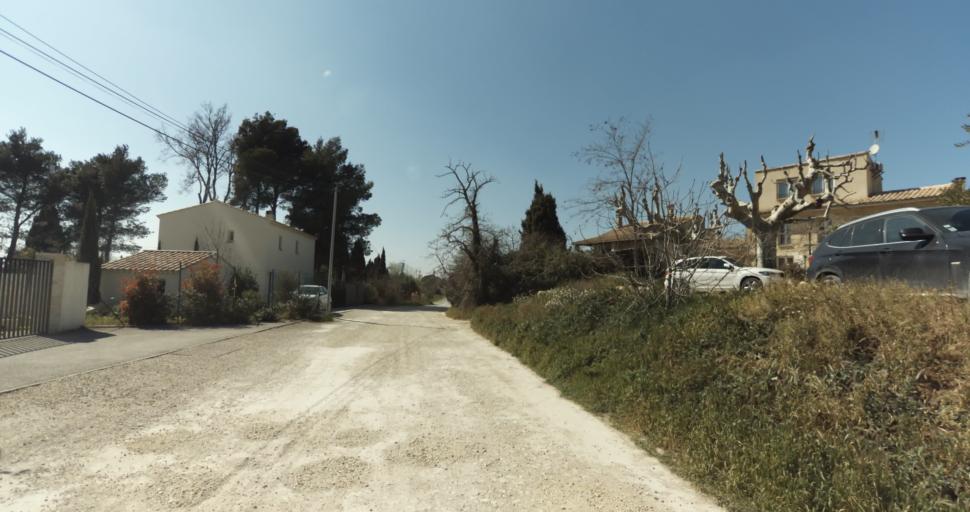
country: FR
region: Provence-Alpes-Cote d'Azur
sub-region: Departement des Bouches-du-Rhone
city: Pelissanne
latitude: 43.6354
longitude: 5.1605
